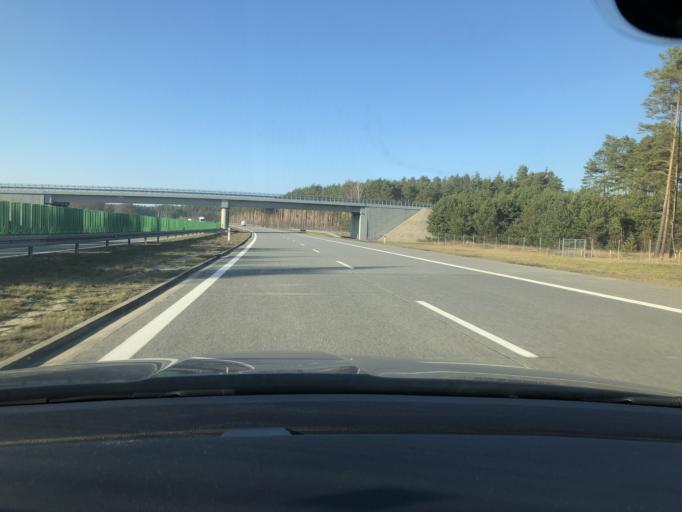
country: PL
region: Lubusz
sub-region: Powiat swiebodzinski
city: Lagow
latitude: 52.3038
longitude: 15.2549
